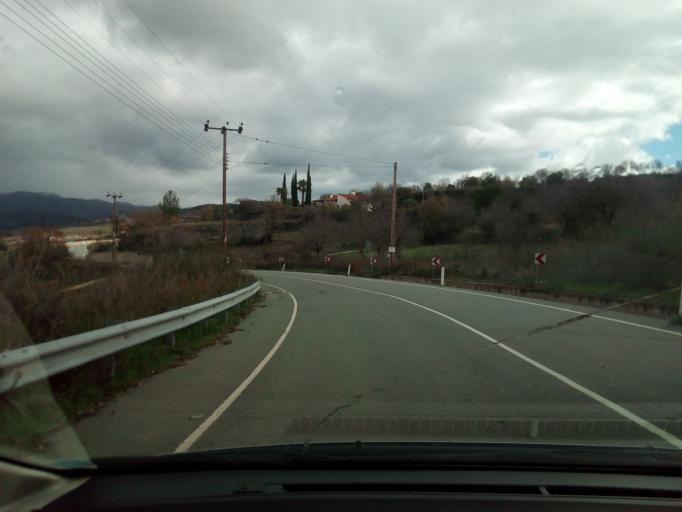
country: CY
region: Pafos
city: Tala
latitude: 34.9327
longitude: 32.5132
